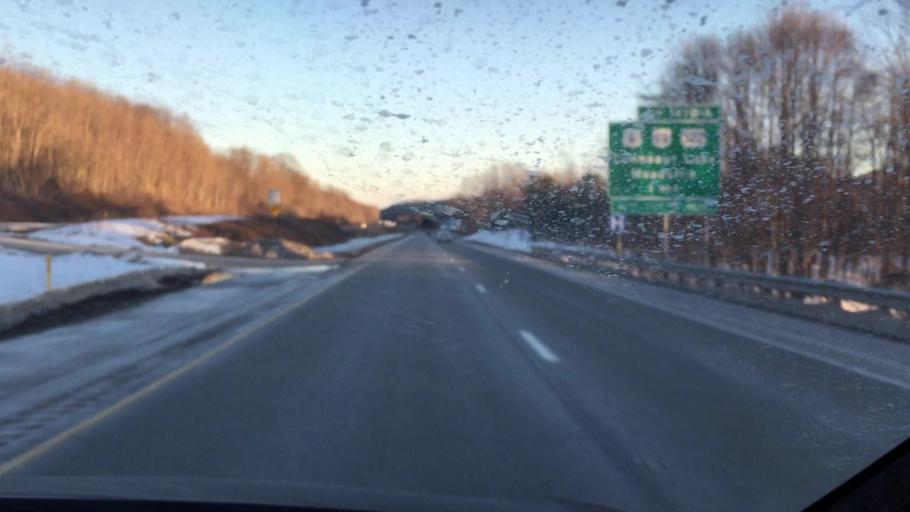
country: US
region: Pennsylvania
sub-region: Crawford County
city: Meadville
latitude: 41.6367
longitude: -80.1966
